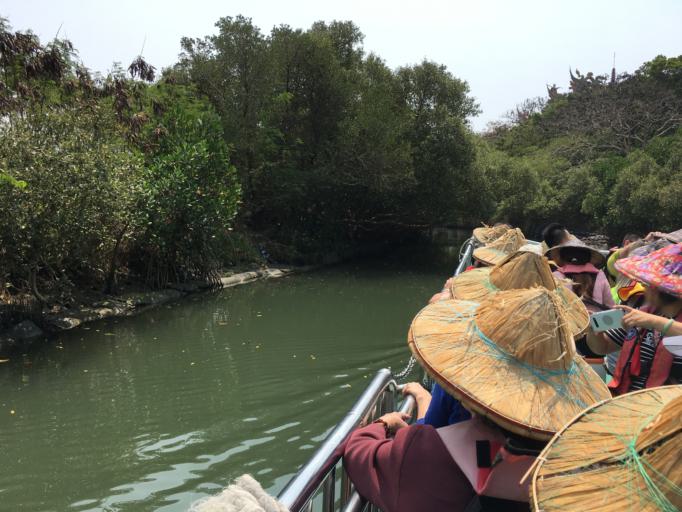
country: TW
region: Taiwan
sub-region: Tainan
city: Tainan
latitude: 23.0210
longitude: 120.1348
